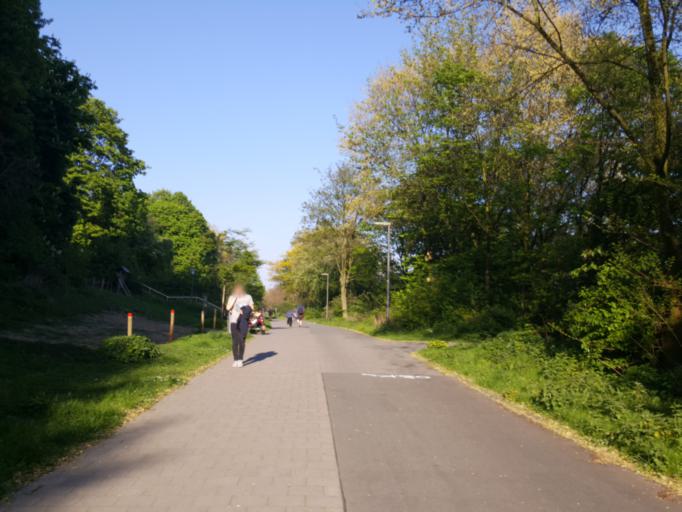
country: DE
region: Hamburg
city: Borgfelde
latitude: 53.5550
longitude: 10.0330
